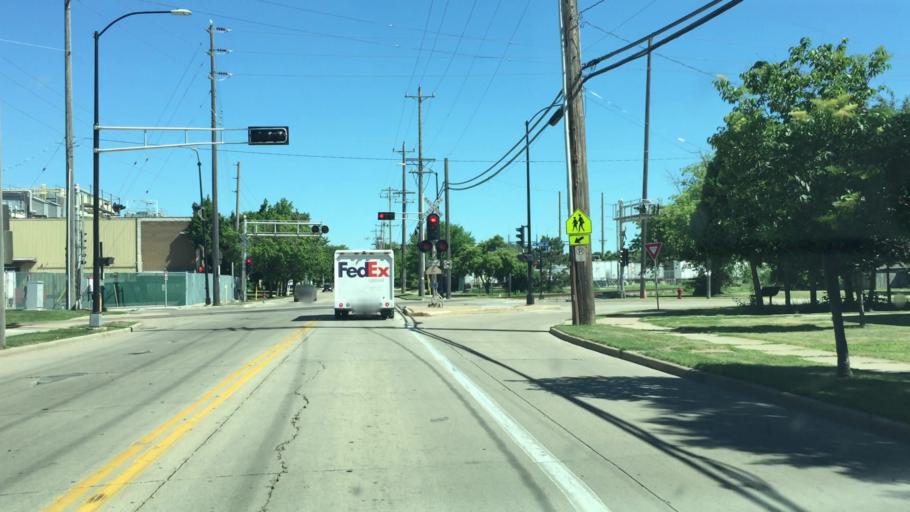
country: US
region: Wisconsin
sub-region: Winnebago County
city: Menasha
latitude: 44.2043
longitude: -88.4531
